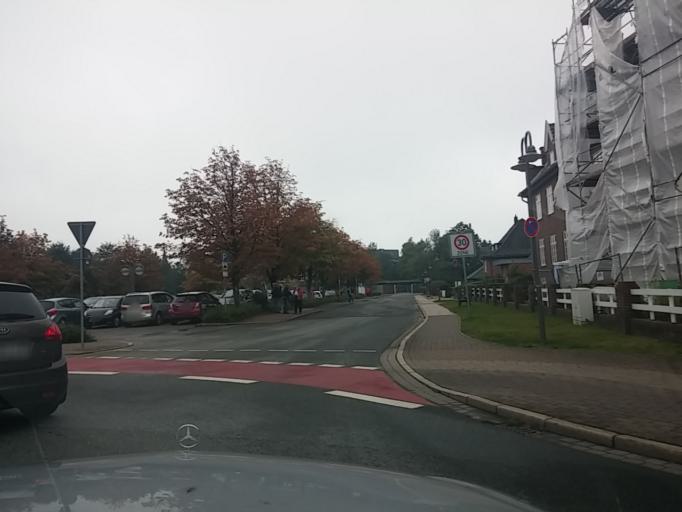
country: DE
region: Schleswig-Holstein
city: Husum
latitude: 54.4747
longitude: 9.0553
